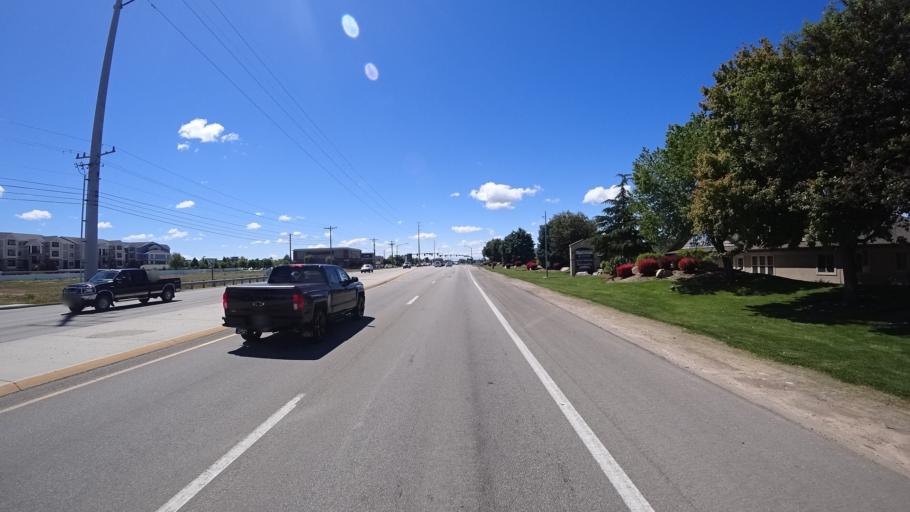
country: US
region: Idaho
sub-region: Ada County
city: Meridian
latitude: 43.6285
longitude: -116.3547
